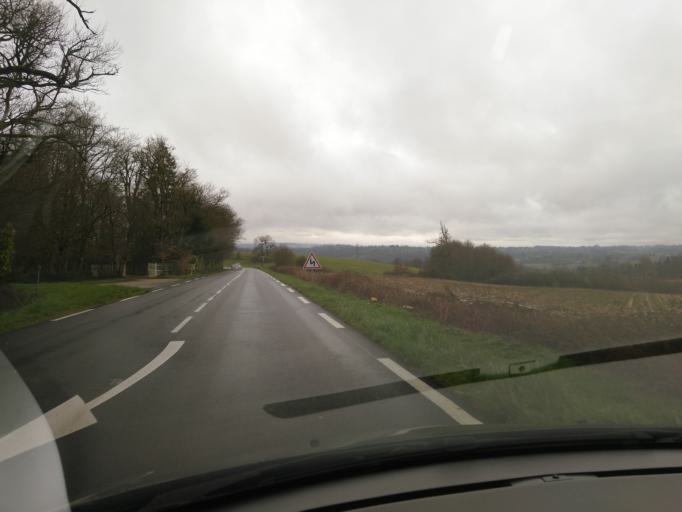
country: FR
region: Limousin
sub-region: Departement de la Haute-Vienne
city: Le Vigen
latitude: 45.7692
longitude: 1.2903
